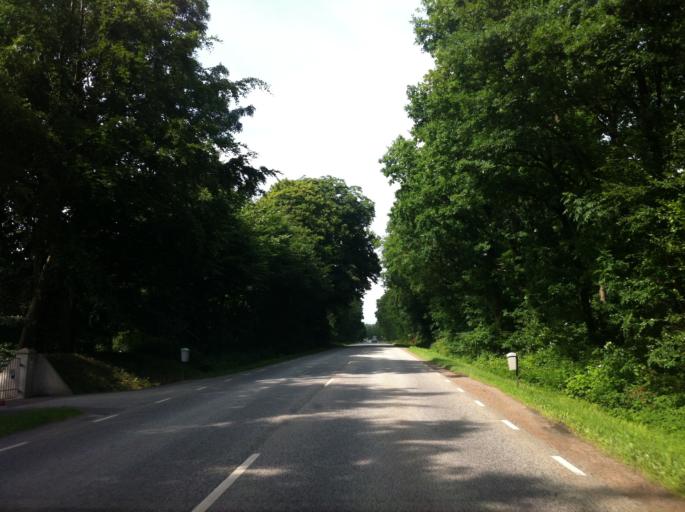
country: SE
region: Skane
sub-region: Skurups Kommun
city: Skurup
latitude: 55.5145
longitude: 13.4334
